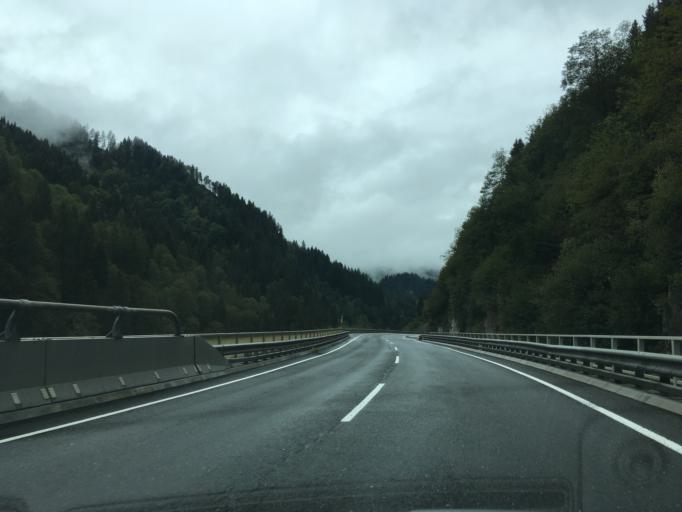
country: AT
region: Salzburg
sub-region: Politischer Bezirk Zell am See
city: Taxenbach
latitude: 47.3007
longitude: 12.9944
